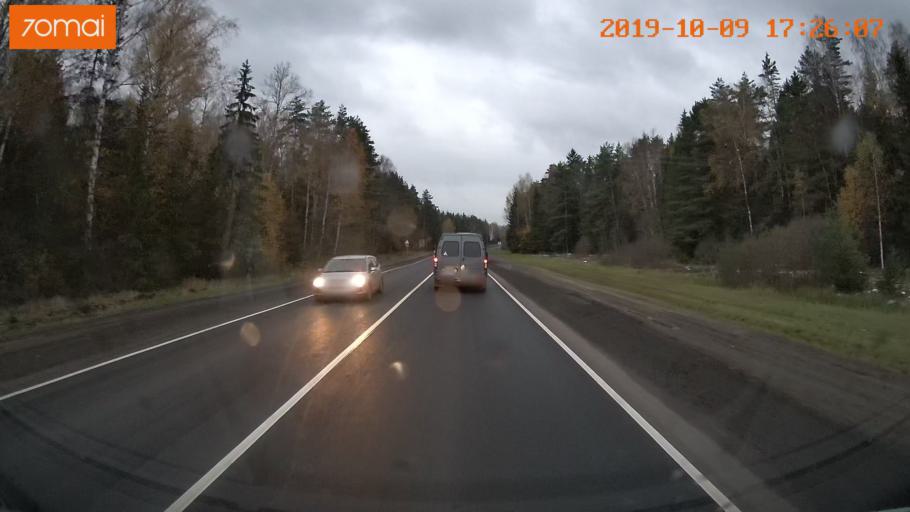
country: RU
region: Ivanovo
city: Furmanov
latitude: 57.1763
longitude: 41.0822
